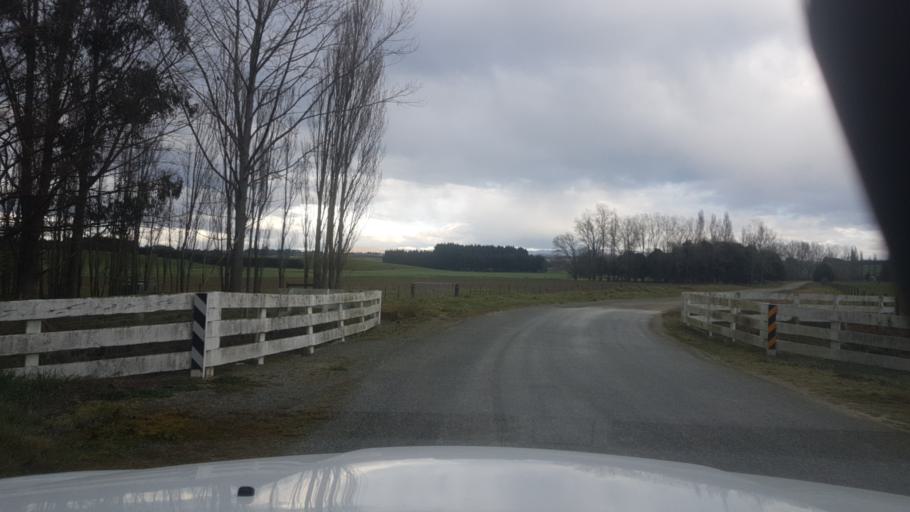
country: NZ
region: Canterbury
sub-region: Timaru District
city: Timaru
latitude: -44.3390
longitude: 171.1943
